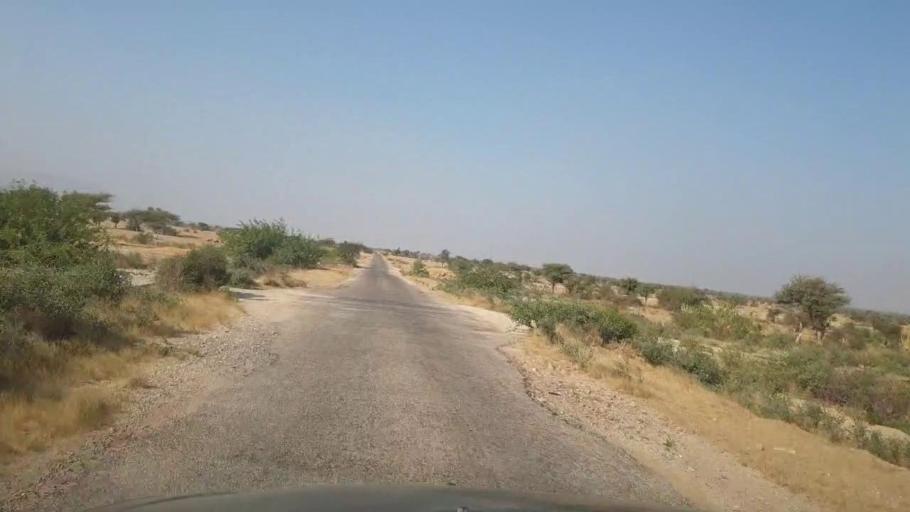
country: PK
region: Sindh
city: Jamshoro
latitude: 25.5746
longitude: 67.8229
